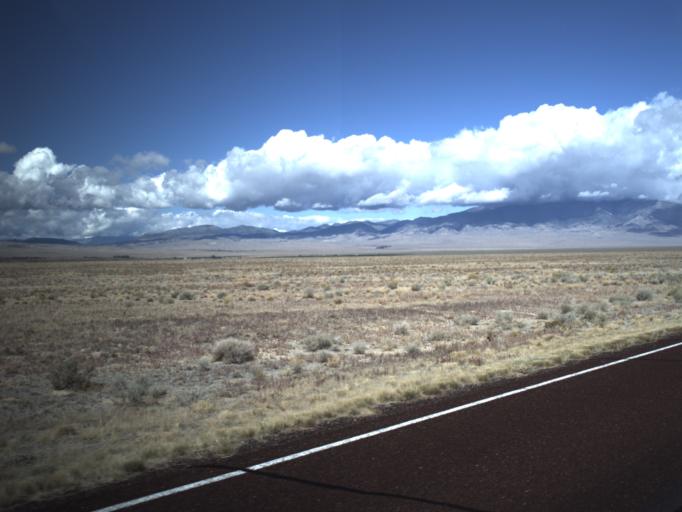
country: US
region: Nevada
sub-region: White Pine County
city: McGill
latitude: 38.9692
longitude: -114.0338
